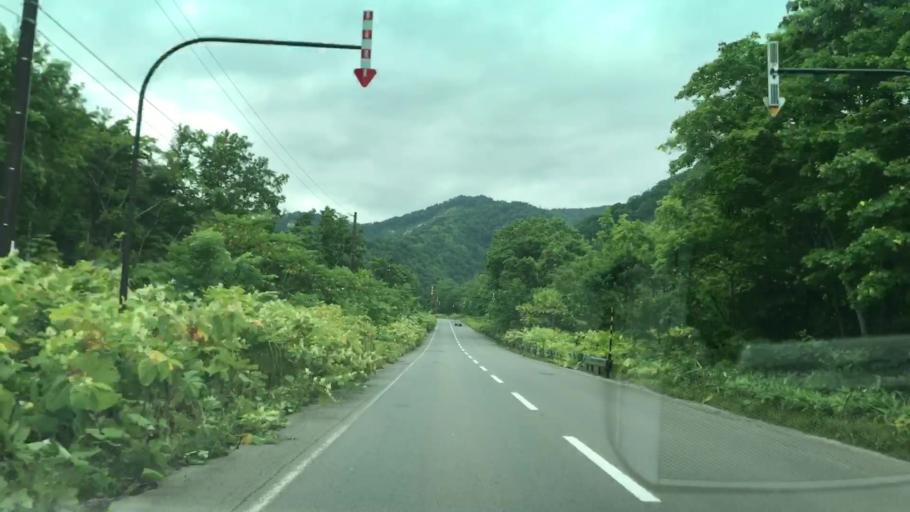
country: JP
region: Hokkaido
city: Yoichi
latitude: 43.0172
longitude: 140.8678
